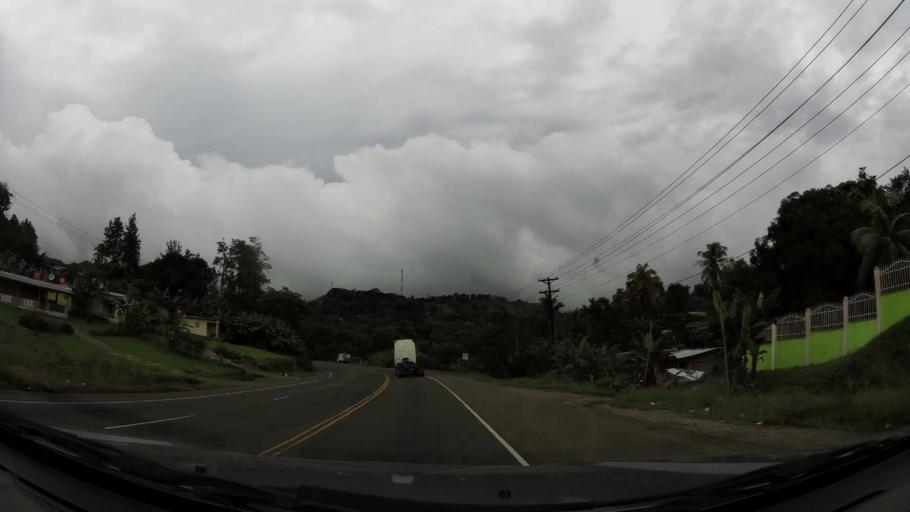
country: PA
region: Colon
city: Nuevo Vigia
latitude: 9.2367
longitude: -79.6318
